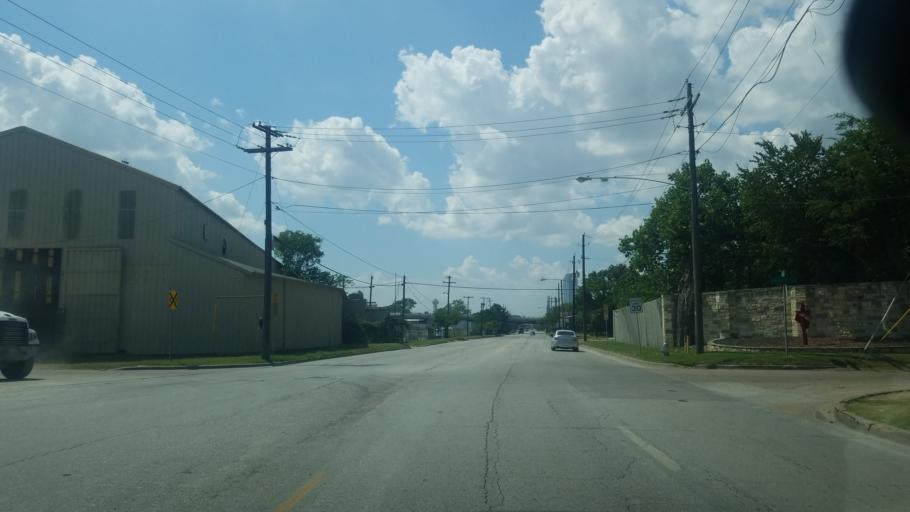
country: US
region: Texas
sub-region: Dallas County
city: Dallas
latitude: 32.7551
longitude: -96.7775
